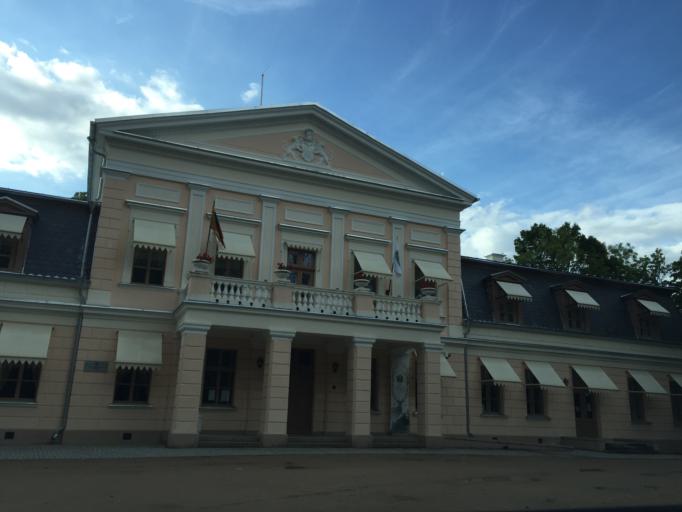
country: LT
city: Zagare
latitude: 56.3621
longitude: 23.2647
